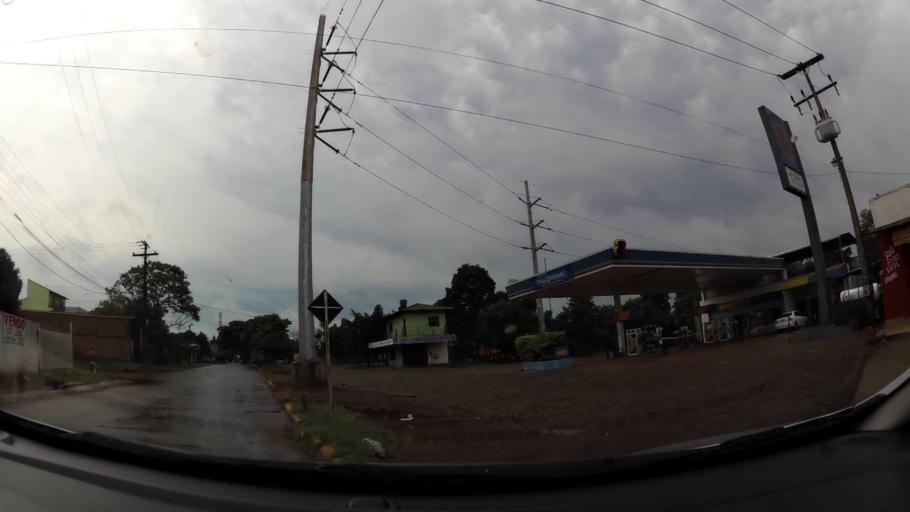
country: PY
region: Alto Parana
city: Presidente Franco
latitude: -25.5242
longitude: -54.6657
